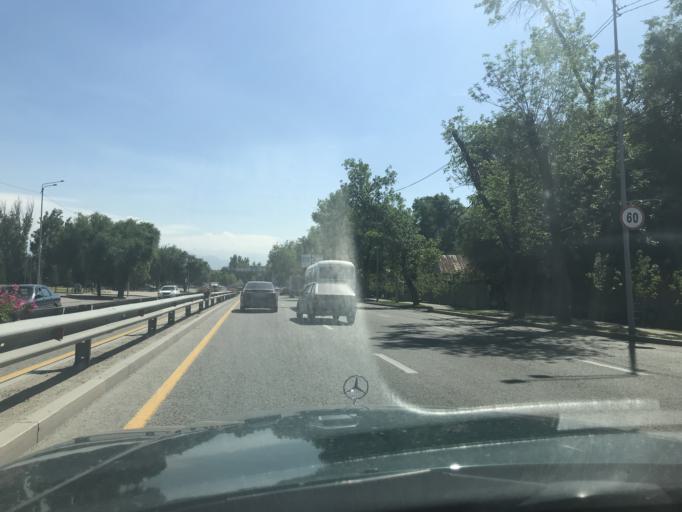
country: KZ
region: Almaty Qalasy
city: Almaty
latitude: 43.2893
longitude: 76.9896
